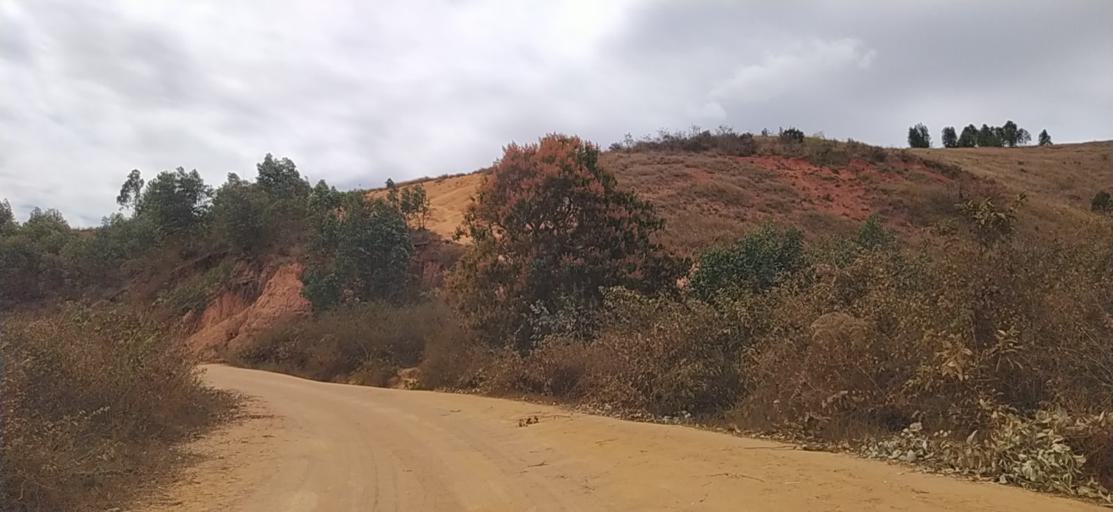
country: MG
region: Alaotra Mangoro
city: Ambatondrazaka
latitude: -18.0007
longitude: 48.2636
